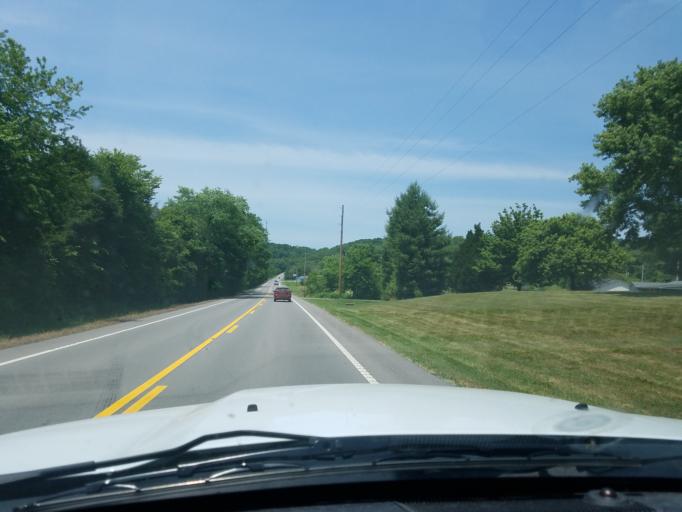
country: US
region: Tennessee
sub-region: Sumner County
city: Westmoreland
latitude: 36.4586
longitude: -86.2678
